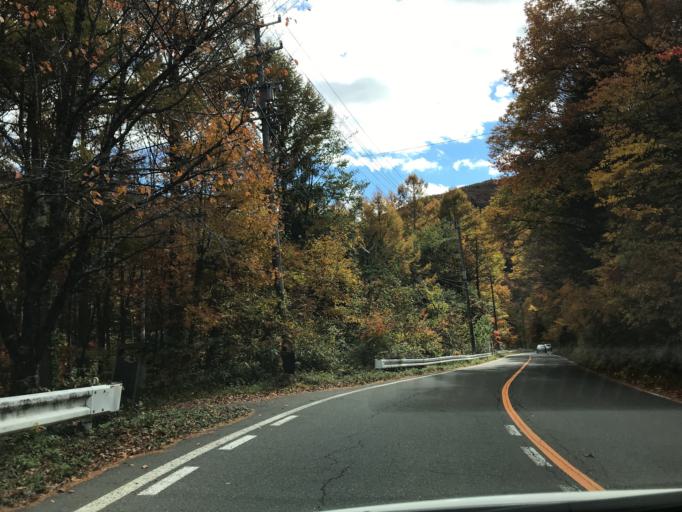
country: JP
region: Nagano
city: Toyoshina
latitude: 36.1377
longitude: 137.6711
